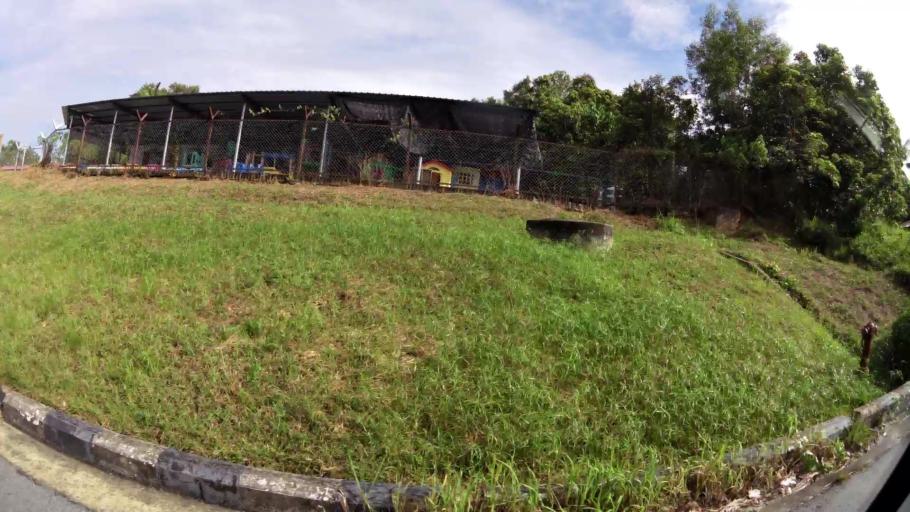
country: BN
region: Brunei and Muara
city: Bandar Seri Begawan
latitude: 4.9006
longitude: 114.8869
